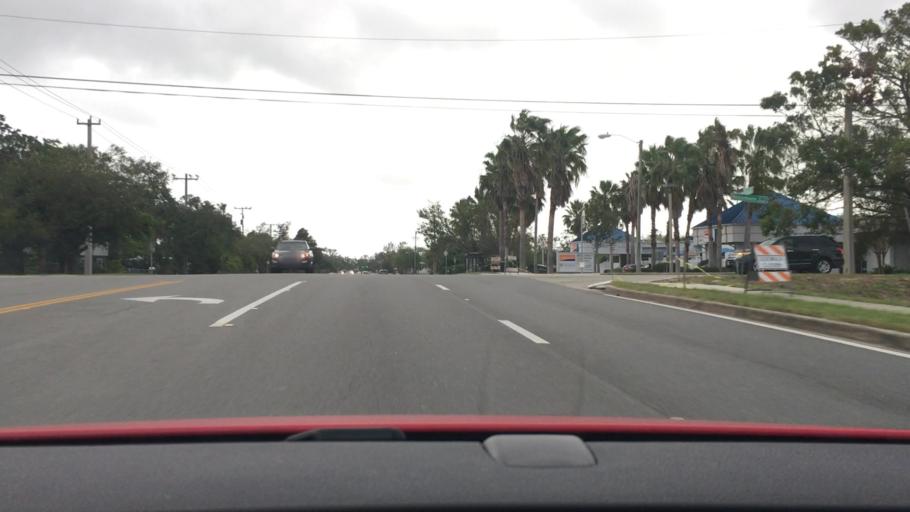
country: US
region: Florida
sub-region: Volusia County
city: Daytona Beach
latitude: 29.2069
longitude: -81.0557
